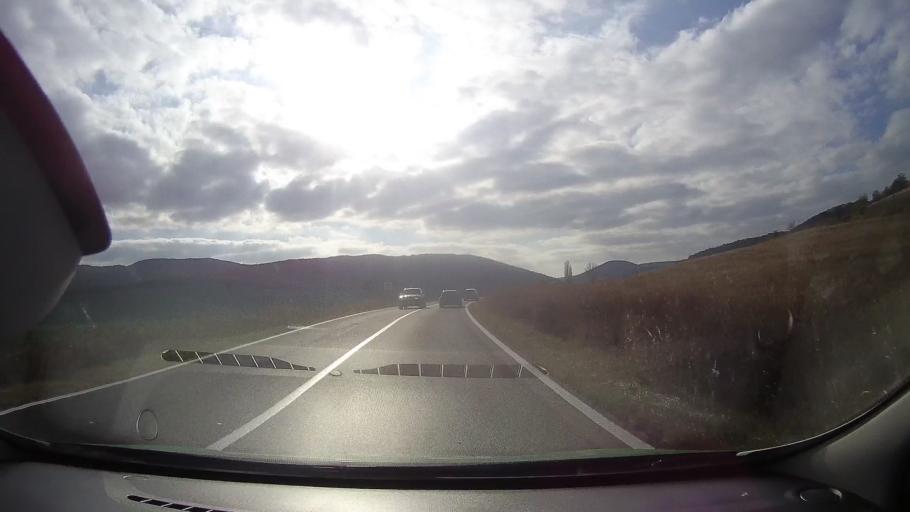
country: RO
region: Tulcea
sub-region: Comuna Nalbant
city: Nicolae Balcescu
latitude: 44.9699
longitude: 28.5385
